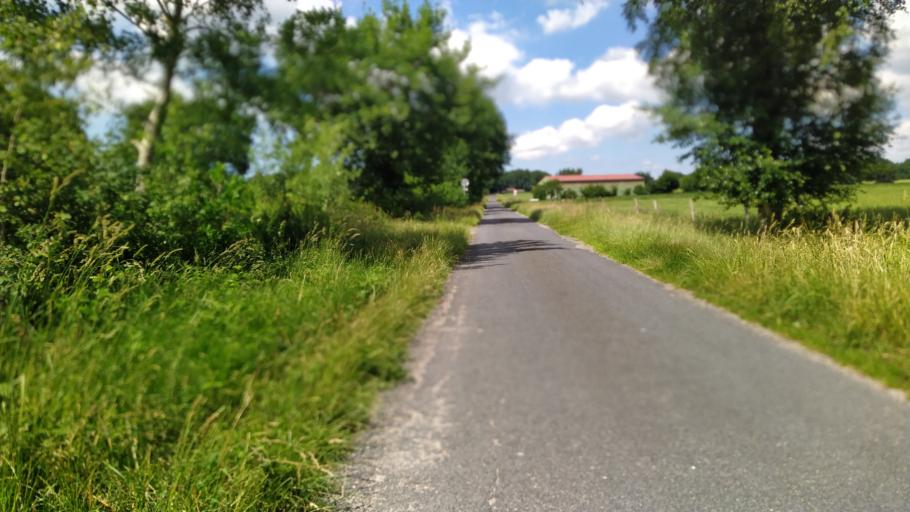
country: DE
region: Lower Saxony
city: Armstorf
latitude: 53.6001
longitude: 9.0760
